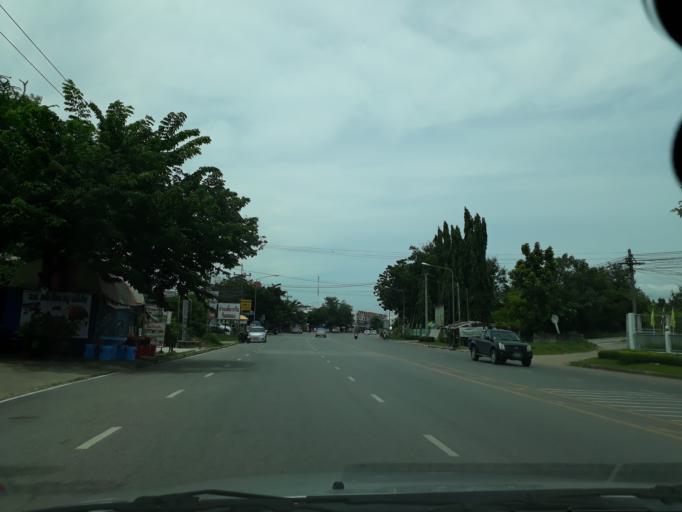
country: TH
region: Khon Kaen
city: Khon Kaen
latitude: 16.4331
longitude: 102.8664
